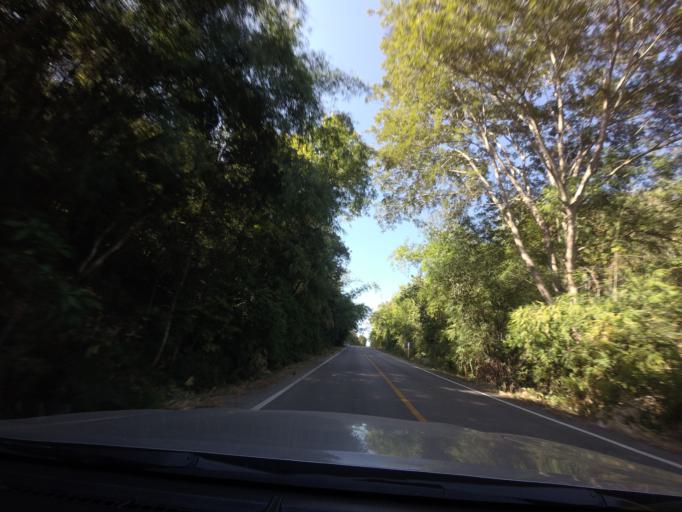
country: TH
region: Lampang
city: Chae Hom
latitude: 18.5476
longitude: 99.6352
